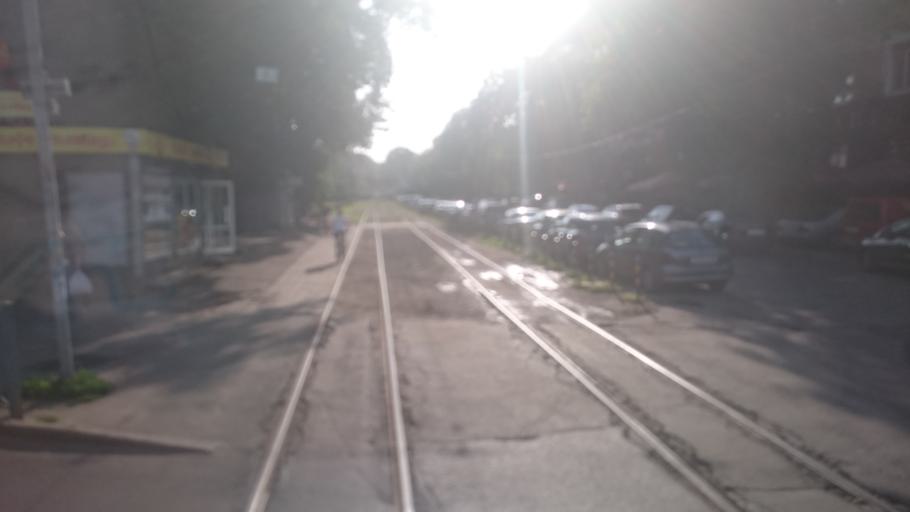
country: RU
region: Kaliningrad
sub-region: Gorod Kaliningrad
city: Kaliningrad
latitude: 54.7285
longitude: 20.4814
